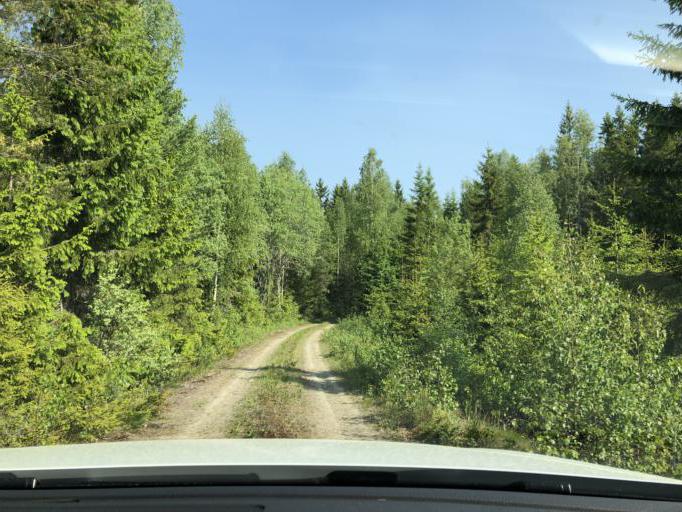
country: SE
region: Dalarna
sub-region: Avesta Kommun
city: Horndal
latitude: 60.2187
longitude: 16.5174
